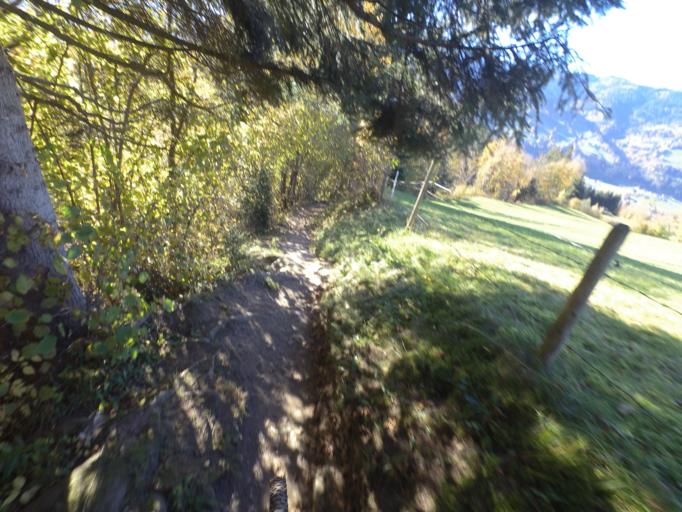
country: AT
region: Salzburg
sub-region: Politischer Bezirk Sankt Johann im Pongau
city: Sankt Johann im Pongau
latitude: 47.3472
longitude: 13.2173
